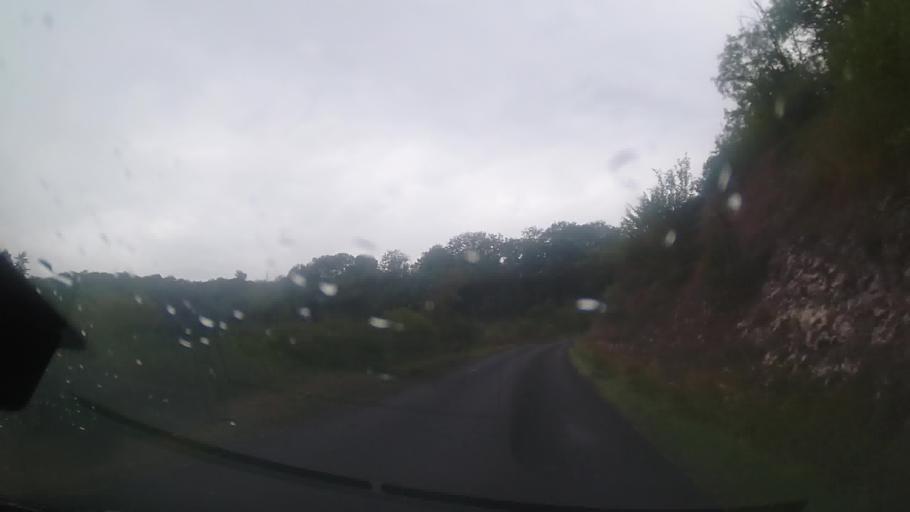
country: FR
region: Aquitaine
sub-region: Departement de la Dordogne
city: Cenac-et-Saint-Julien
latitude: 44.7977
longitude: 1.1929
